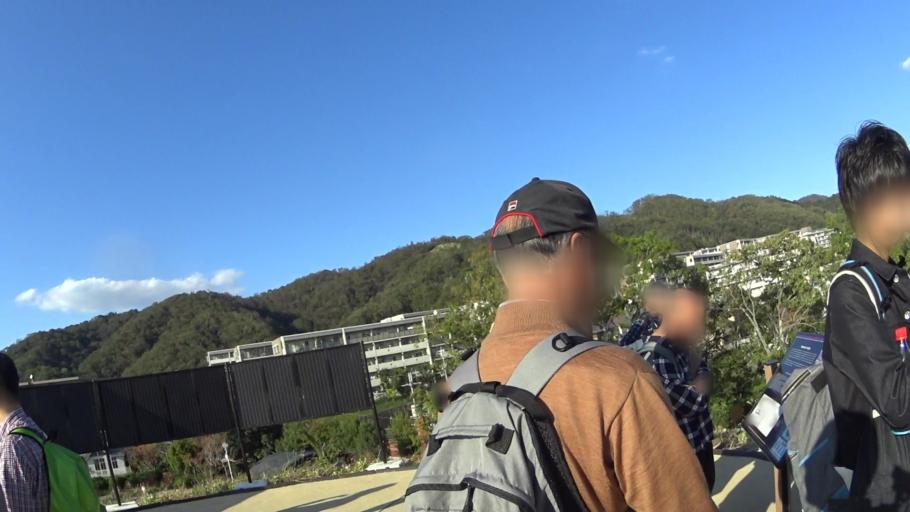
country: JP
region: Osaka
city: Ikeda
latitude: 34.8261
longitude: 135.4340
